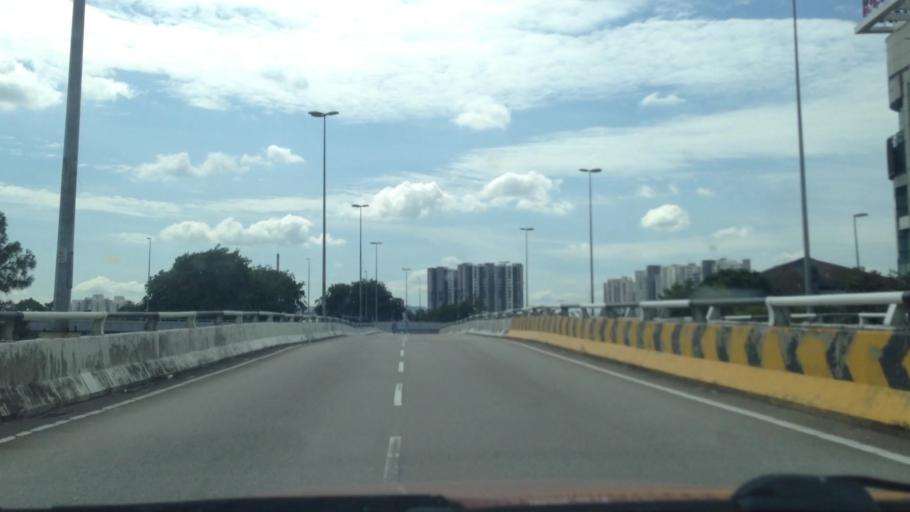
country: MY
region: Kuala Lumpur
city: Kuala Lumpur
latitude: 3.0918
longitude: 101.6887
